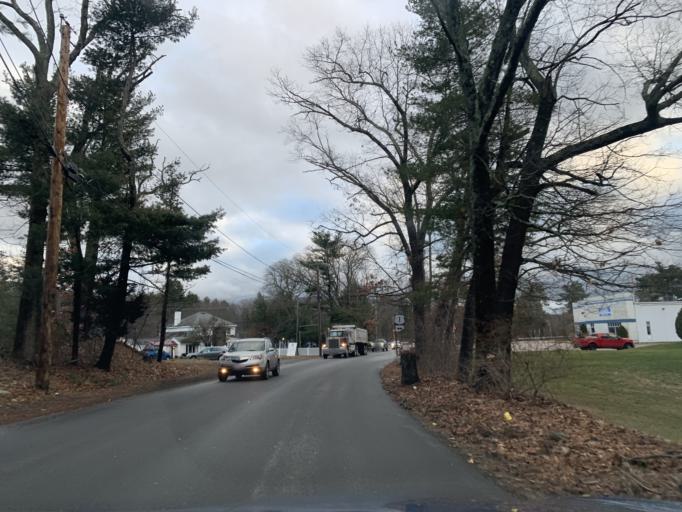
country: US
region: Massachusetts
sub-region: Norfolk County
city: Foxborough
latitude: 42.0813
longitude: -71.2825
